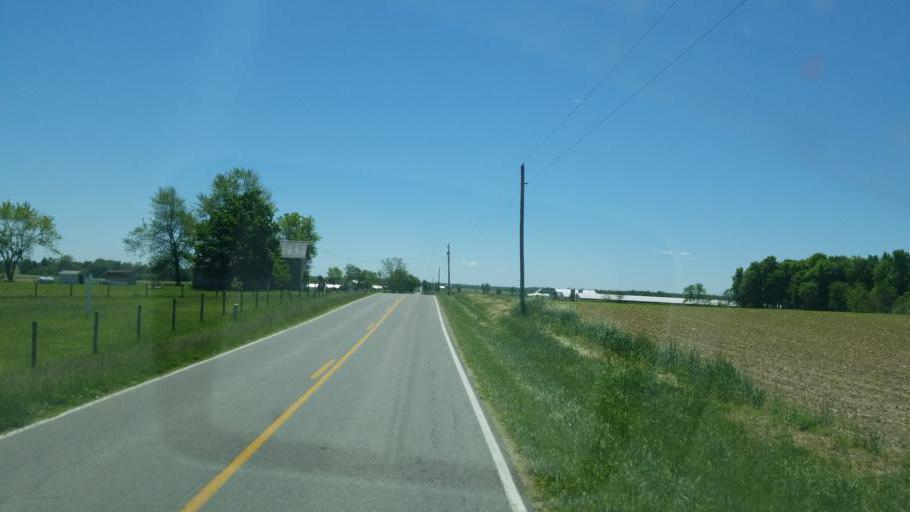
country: US
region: Indiana
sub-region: Randolph County
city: Union City
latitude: 40.3073
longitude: -84.8037
